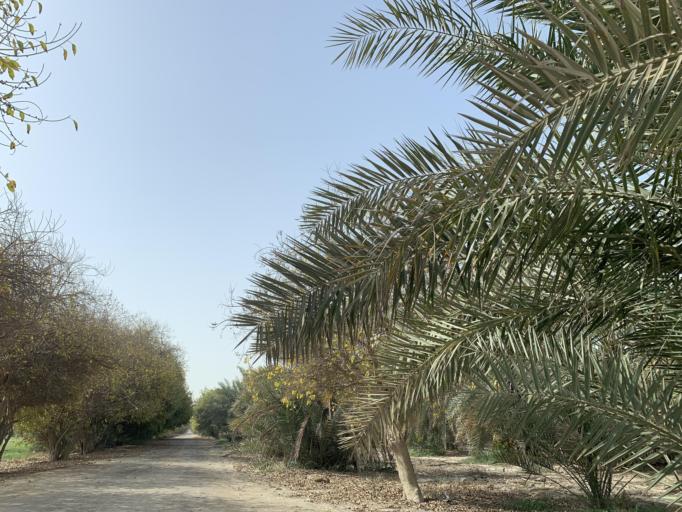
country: BH
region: Northern
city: Madinat `Isa
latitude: 26.1685
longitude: 50.5291
